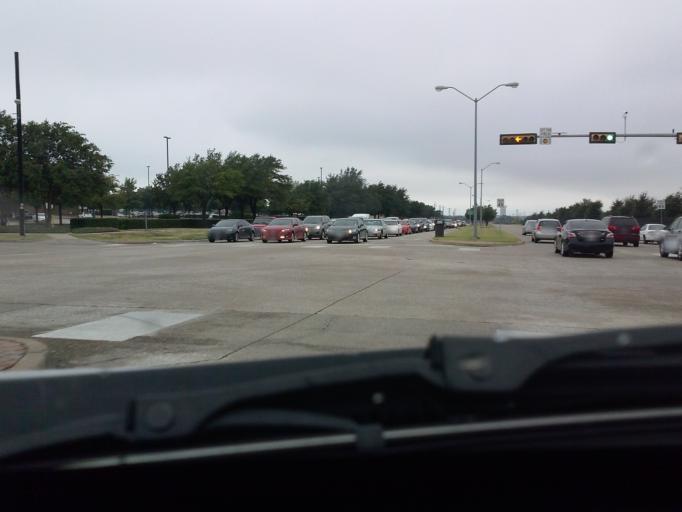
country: US
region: Texas
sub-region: Collin County
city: Plano
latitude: 33.0565
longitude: -96.7892
